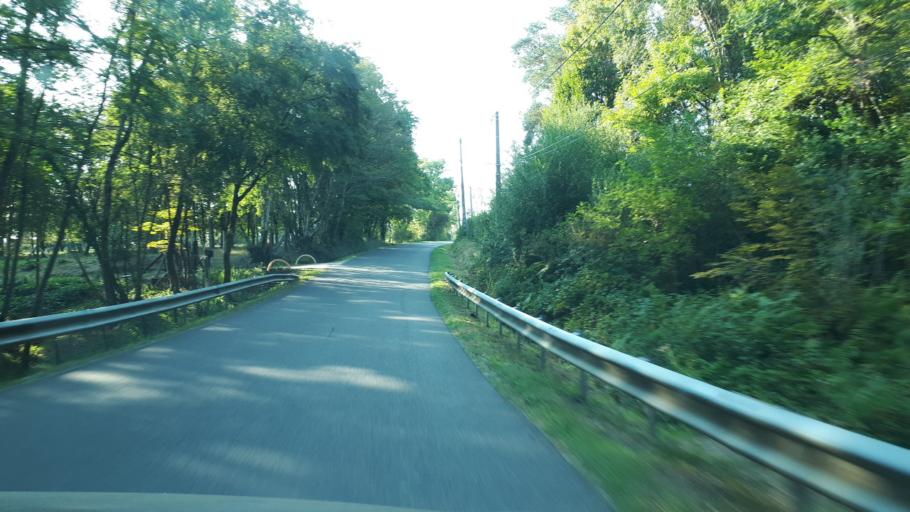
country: FR
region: Centre
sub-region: Departement du Cher
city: Saint-Eloy-de-Gy
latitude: 47.2228
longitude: 2.3308
